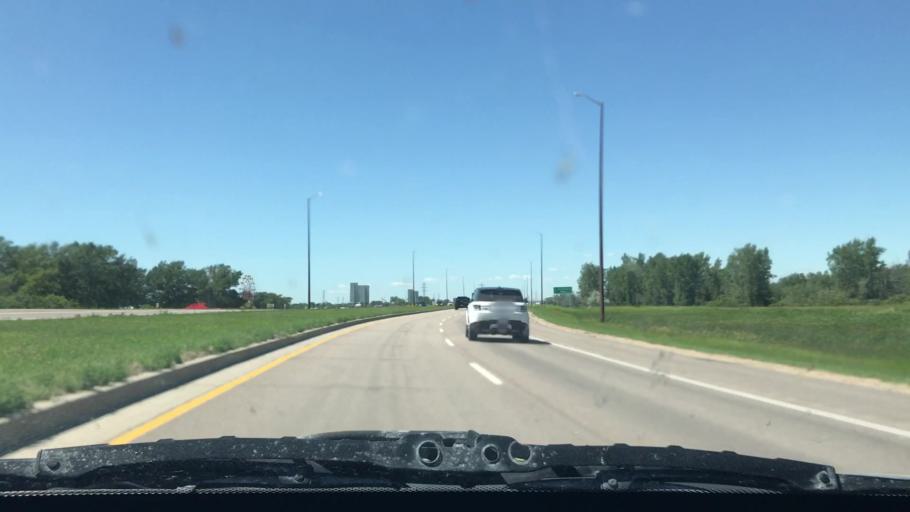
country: CA
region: Manitoba
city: Winnipeg
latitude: 49.8364
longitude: -96.9750
